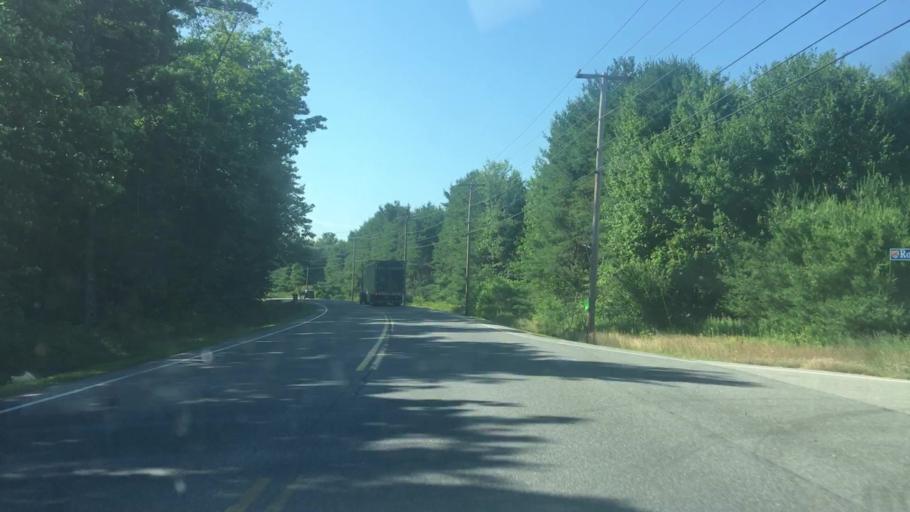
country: US
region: Maine
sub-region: York County
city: Buxton
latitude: 43.5633
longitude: -70.4988
